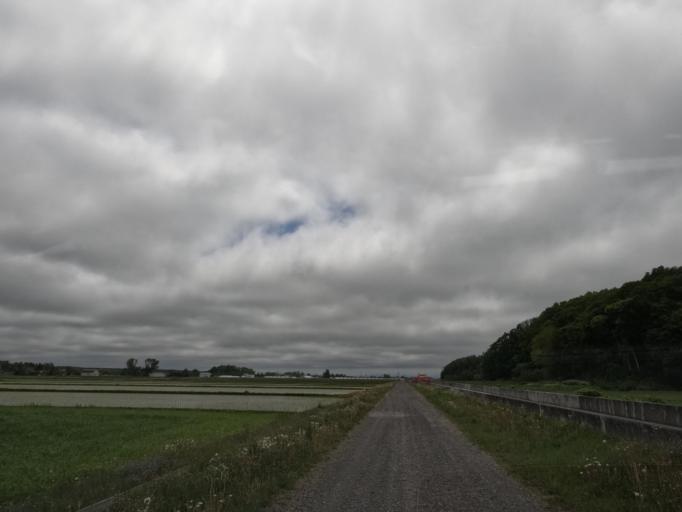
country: JP
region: Hokkaido
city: Tobetsu
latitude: 43.2691
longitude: 141.5237
